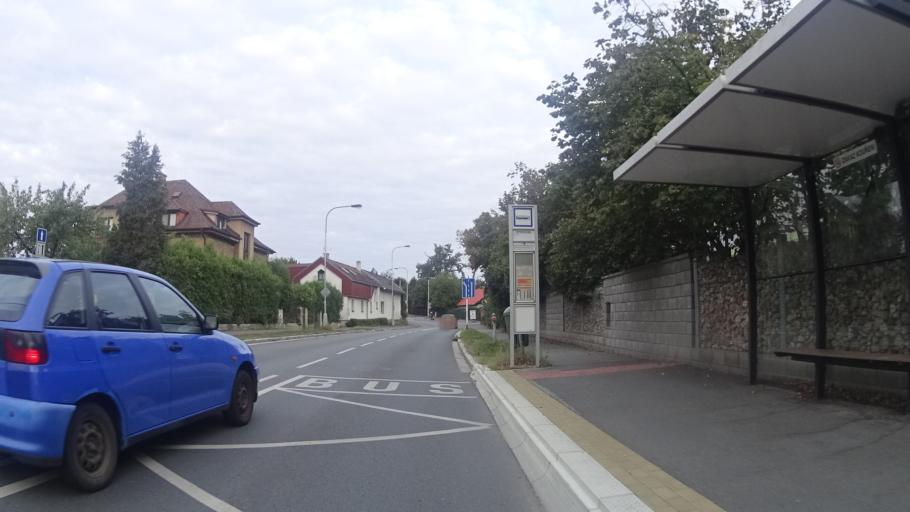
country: CZ
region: Kralovehradecky
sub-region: Okres Hradec Kralove
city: Hradec Kralove
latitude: 50.2041
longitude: 15.8508
